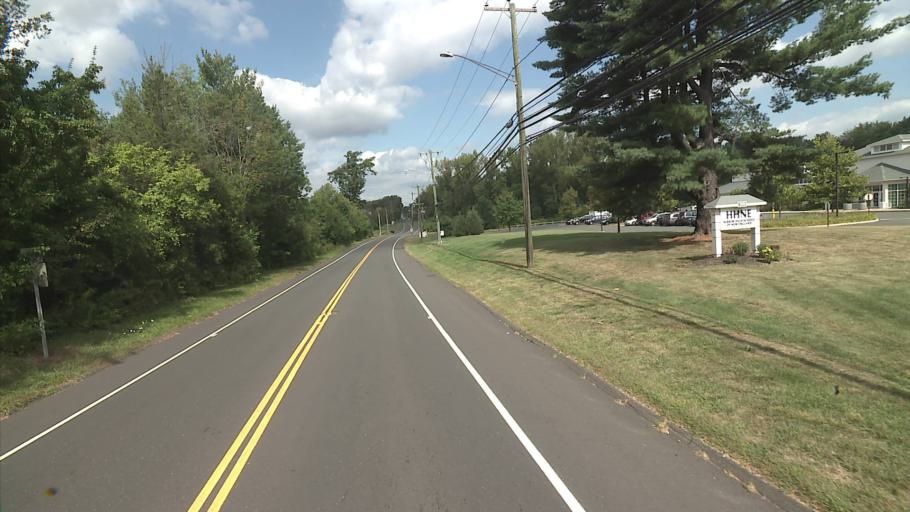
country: US
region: Connecticut
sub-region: Hartford County
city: Blue Hills
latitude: 41.7990
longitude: -72.7232
